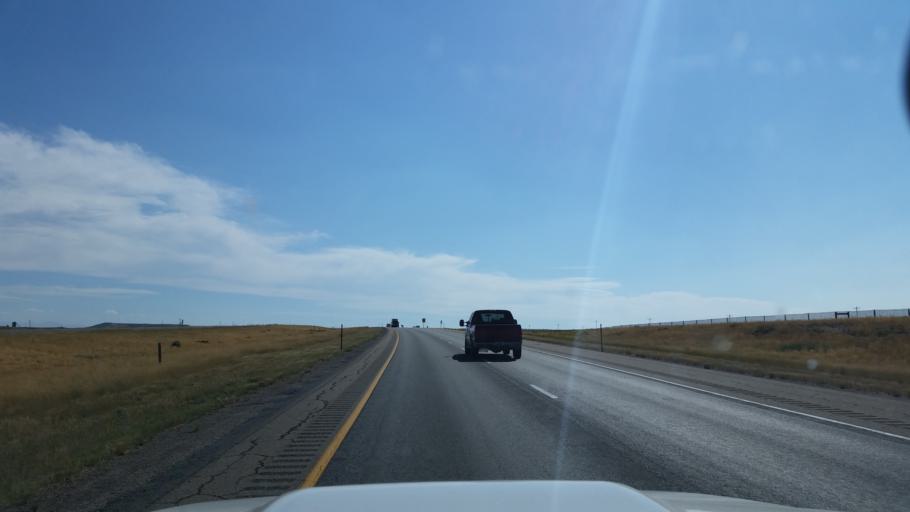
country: US
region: Wyoming
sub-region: Uinta County
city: Lyman
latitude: 41.4975
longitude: -110.0091
